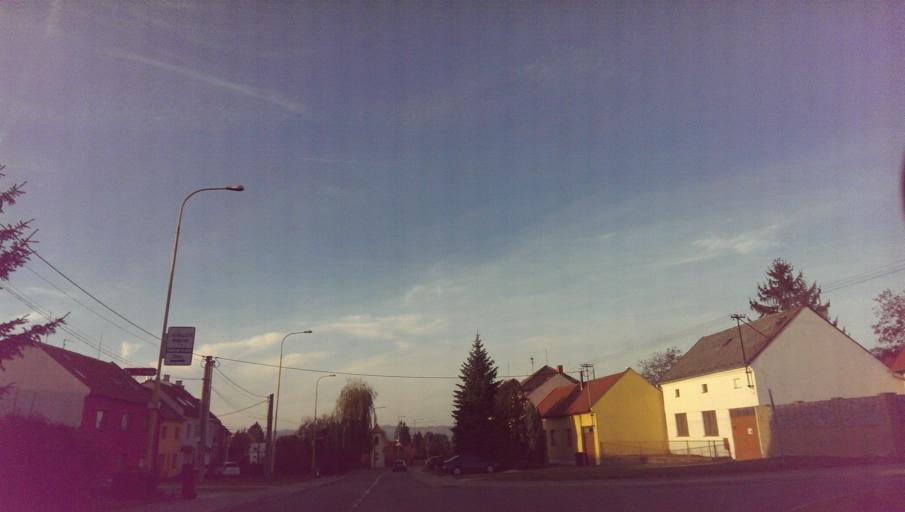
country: CZ
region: Zlin
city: Kunovice
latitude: 49.0622
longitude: 17.4825
